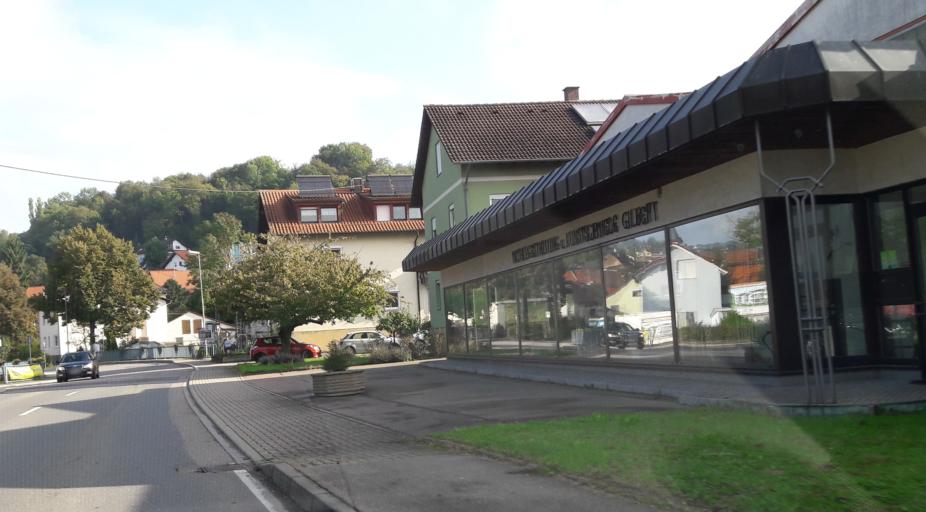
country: DE
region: Baden-Wuerttemberg
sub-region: Karlsruhe Region
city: Sinsheim
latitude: 49.2478
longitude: 8.9041
